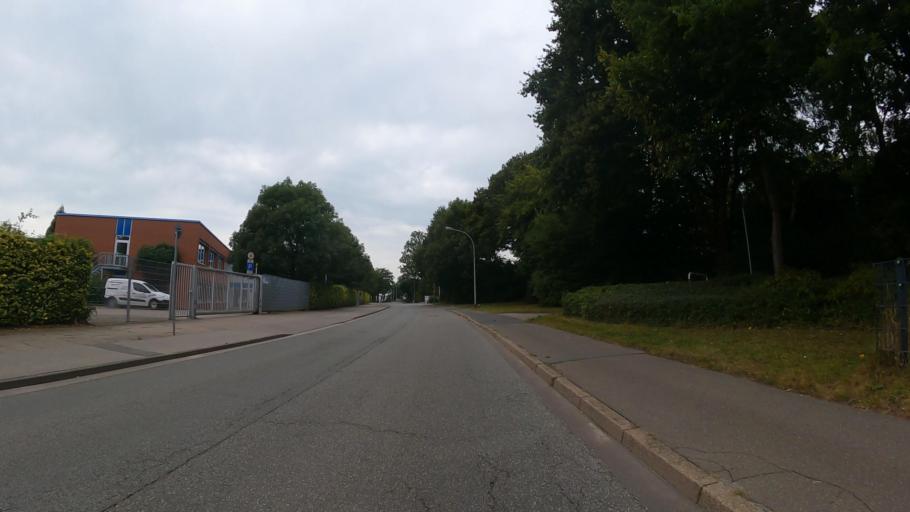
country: DE
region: Schleswig-Holstein
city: Pinneberg
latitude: 53.6645
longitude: 9.7827
